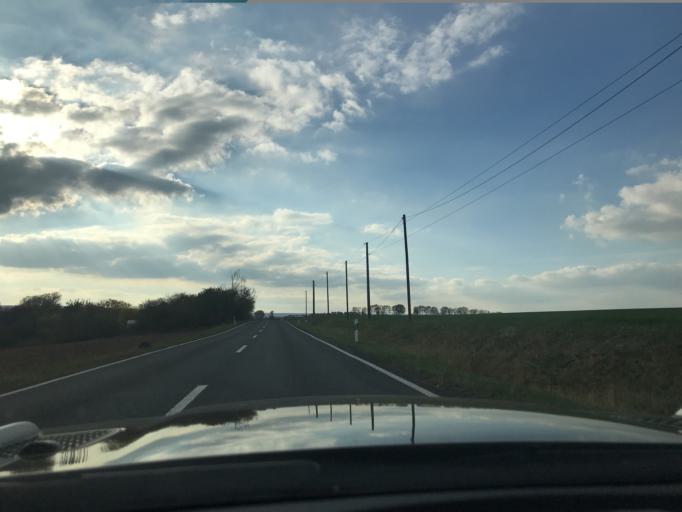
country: DE
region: Thuringia
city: Schonstedt
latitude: 51.1193
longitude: 10.5591
